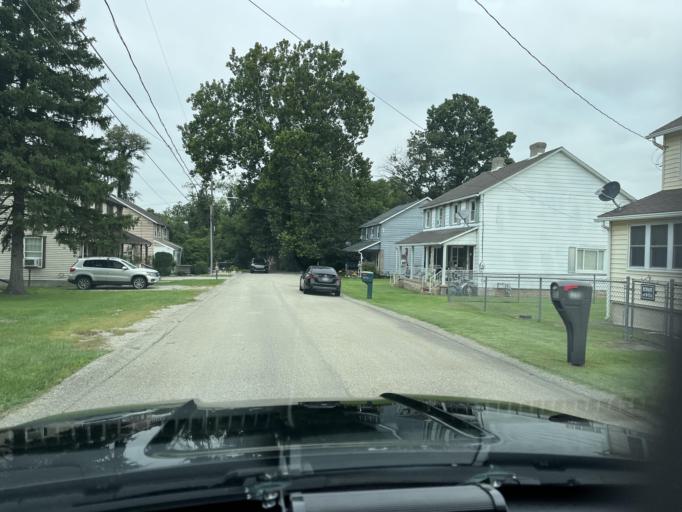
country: US
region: Pennsylvania
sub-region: Fayette County
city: Hopwood
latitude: 39.8767
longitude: -79.7030
